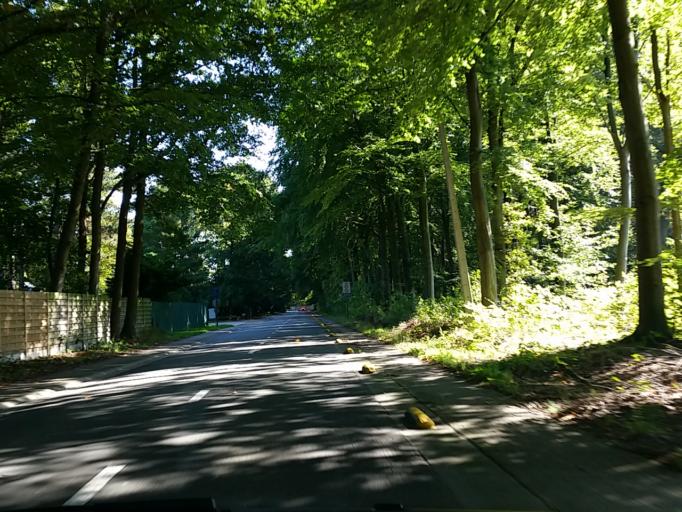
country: BE
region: Flanders
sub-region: Provincie Vlaams-Brabant
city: Kampenhout
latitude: 50.9799
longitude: 4.5233
